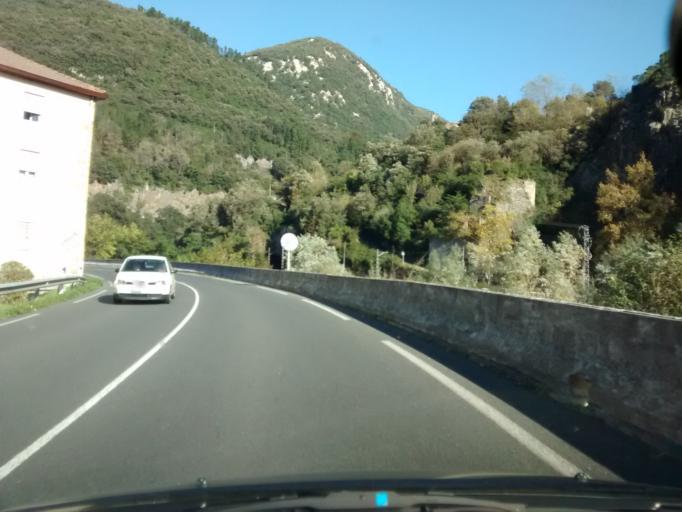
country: ES
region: Basque Country
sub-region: Provincia de Guipuzcoa
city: Mendaro
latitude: 43.2539
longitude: -2.3870
